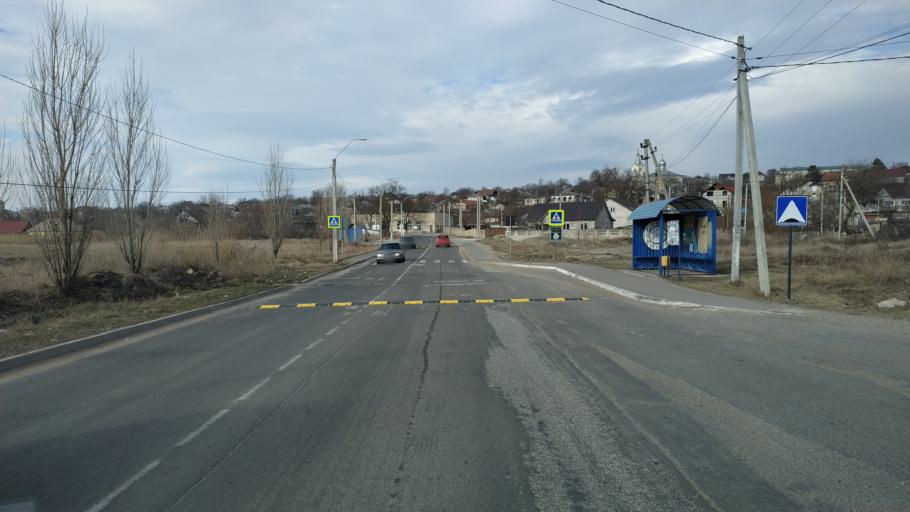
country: MD
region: Laloveni
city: Ialoveni
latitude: 46.9376
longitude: 28.7845
